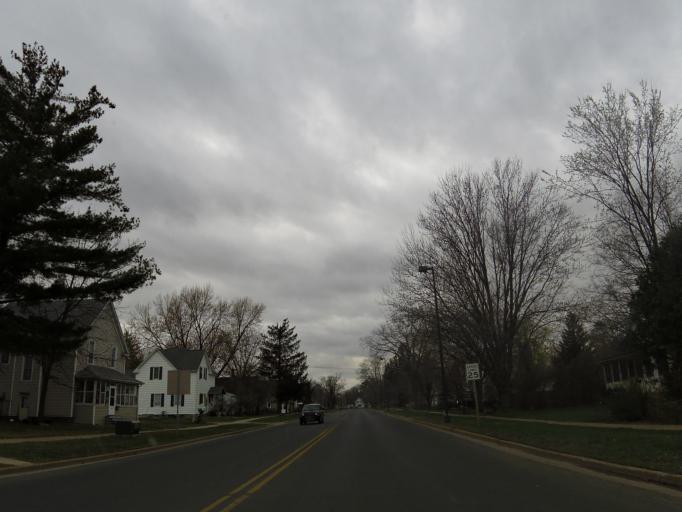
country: US
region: Wisconsin
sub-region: Saint Croix County
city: New Richmond
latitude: 45.1193
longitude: -92.5393
